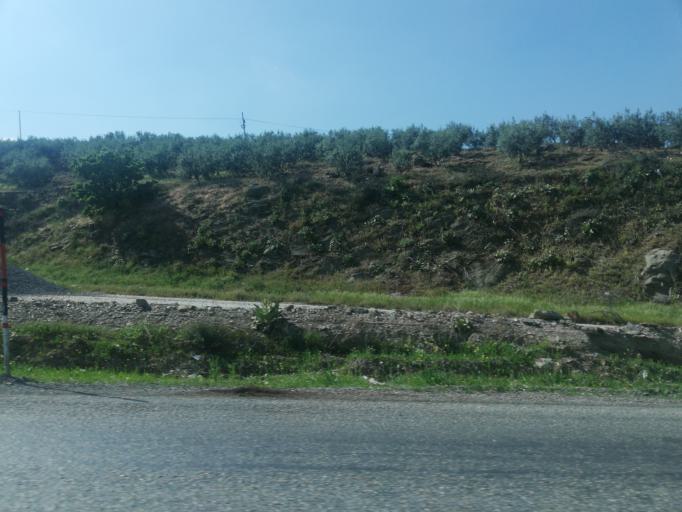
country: TR
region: Manisa
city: Sarigol
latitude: 38.2289
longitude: 28.6690
